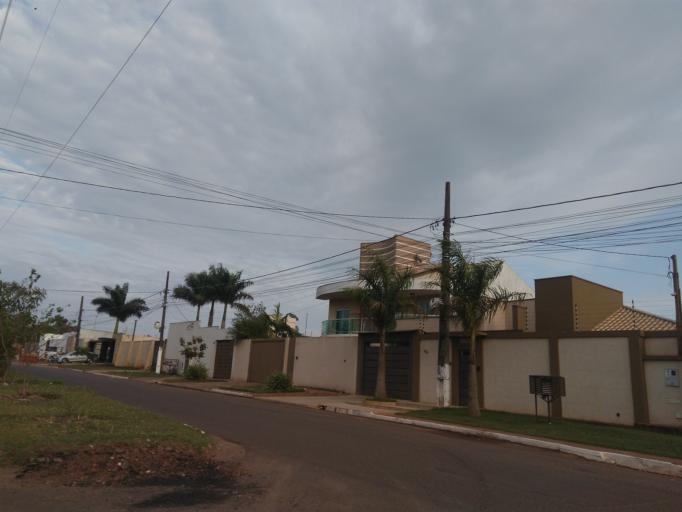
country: BR
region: Mato Grosso do Sul
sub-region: Ponta Pora
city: Ponta Pora
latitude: -22.5264
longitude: -55.7294
